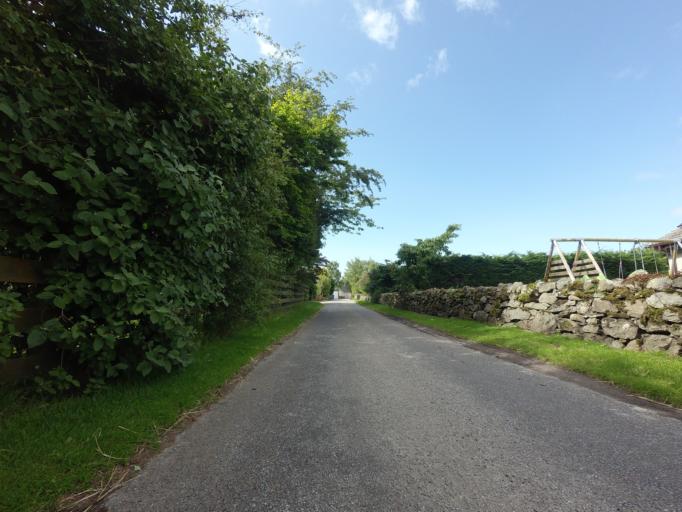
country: GB
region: Scotland
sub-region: Highland
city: Nairn
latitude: 57.5392
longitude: -3.8662
